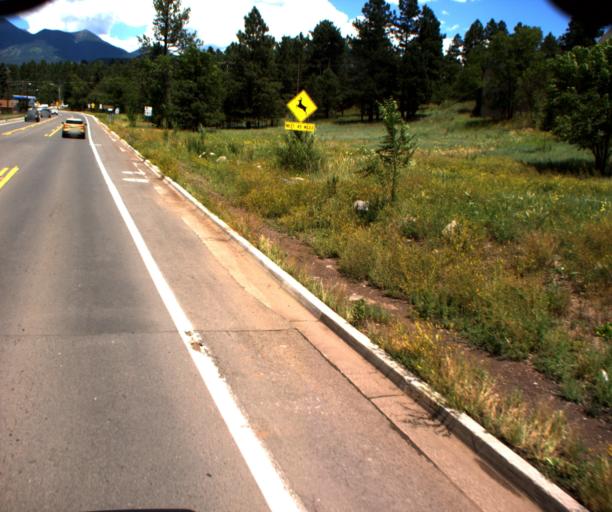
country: US
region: Arizona
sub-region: Coconino County
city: Flagstaff
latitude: 35.2078
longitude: -111.6485
